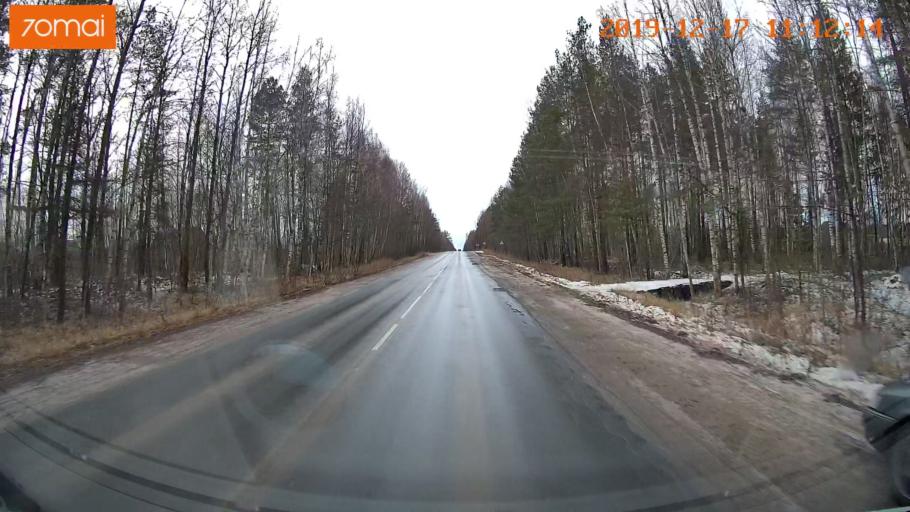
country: RU
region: Vladimir
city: Gus'-Khrustal'nyy
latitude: 55.5785
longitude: 40.6304
